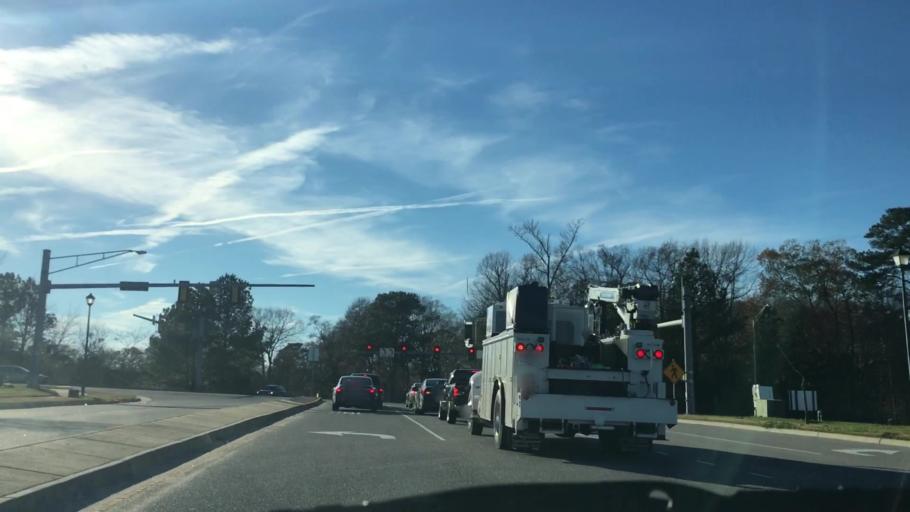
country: US
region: Virginia
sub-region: City of Portsmouth
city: Portsmouth Heights
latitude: 36.8707
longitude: -76.4224
